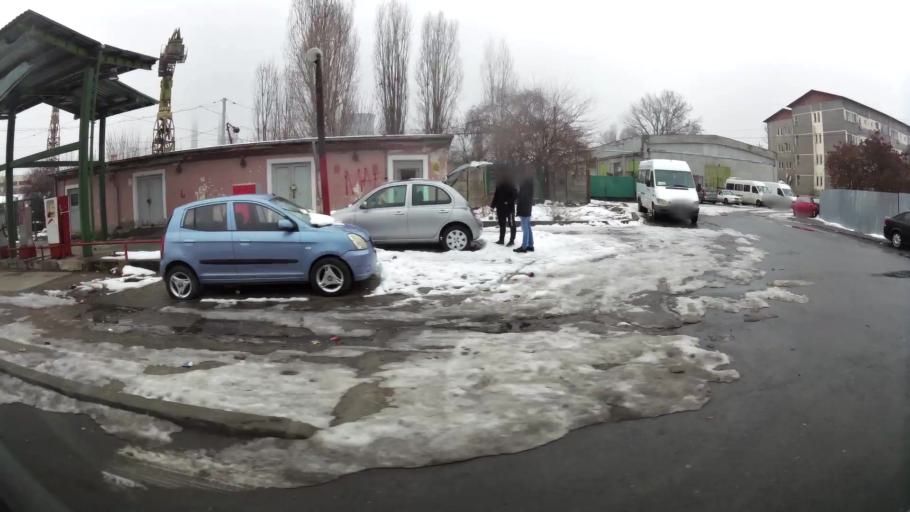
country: RO
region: Ilfov
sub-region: Comuna Popesti-Leordeni
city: Popesti-Leordeni
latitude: 44.4067
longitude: 26.1625
